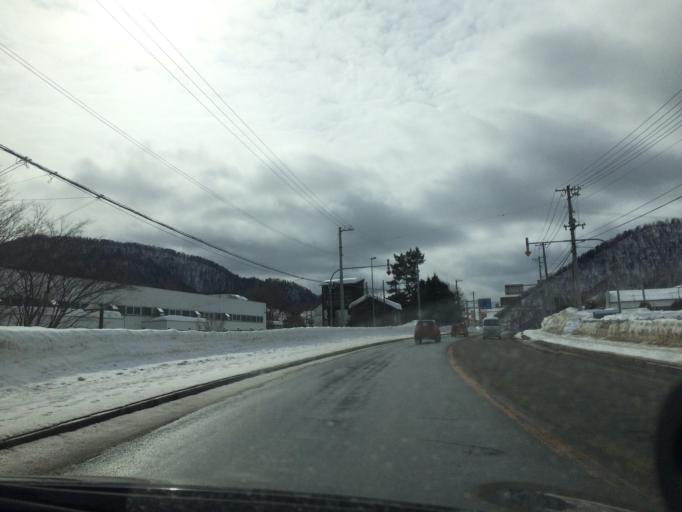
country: JP
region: Hokkaido
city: Iwamizawa
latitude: 42.9410
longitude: 142.0430
